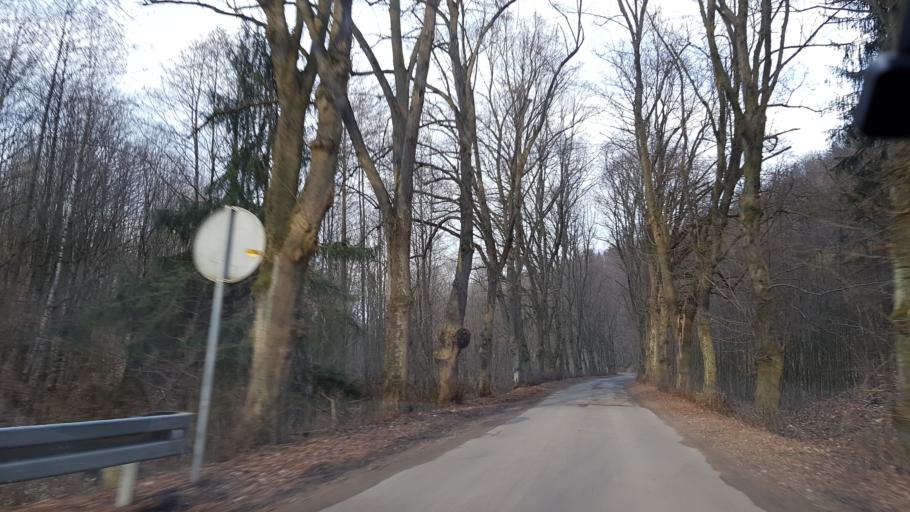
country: PL
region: Lower Silesian Voivodeship
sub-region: Powiat zabkowicki
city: Zloty Stok
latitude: 50.4759
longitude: 16.8097
